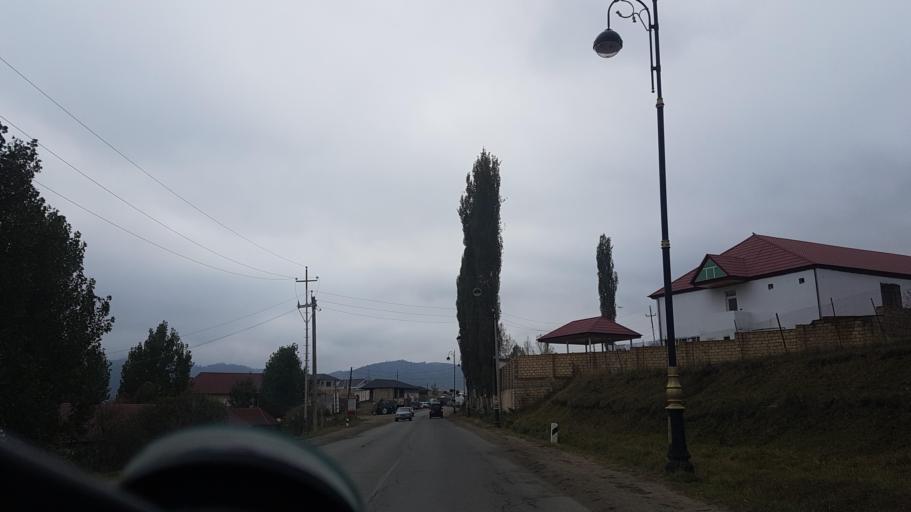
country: AZ
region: Gadabay Rayon
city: Ariqdam
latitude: 40.5940
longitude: 45.8109
